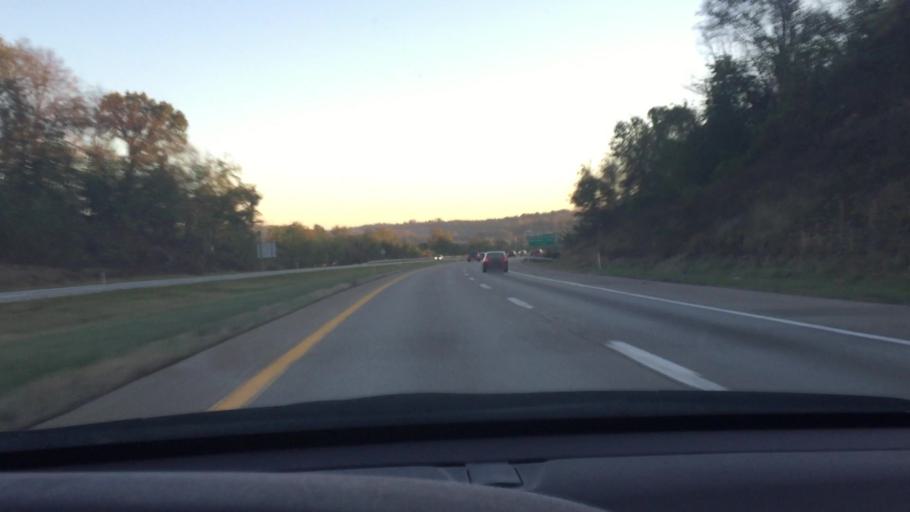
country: US
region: Pennsylvania
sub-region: Washington County
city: Washington
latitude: 40.2041
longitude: -80.2479
